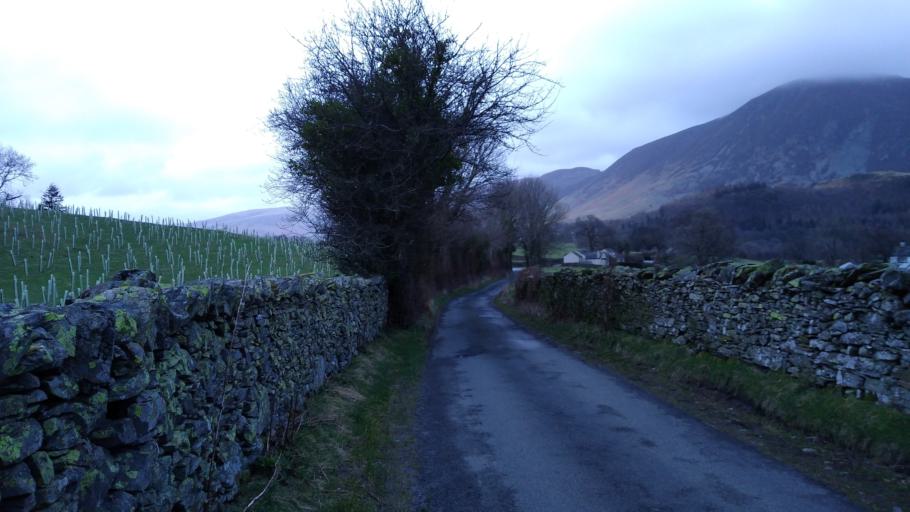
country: GB
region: England
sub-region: Cumbria
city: Cockermouth
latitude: 54.5767
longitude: -3.3291
